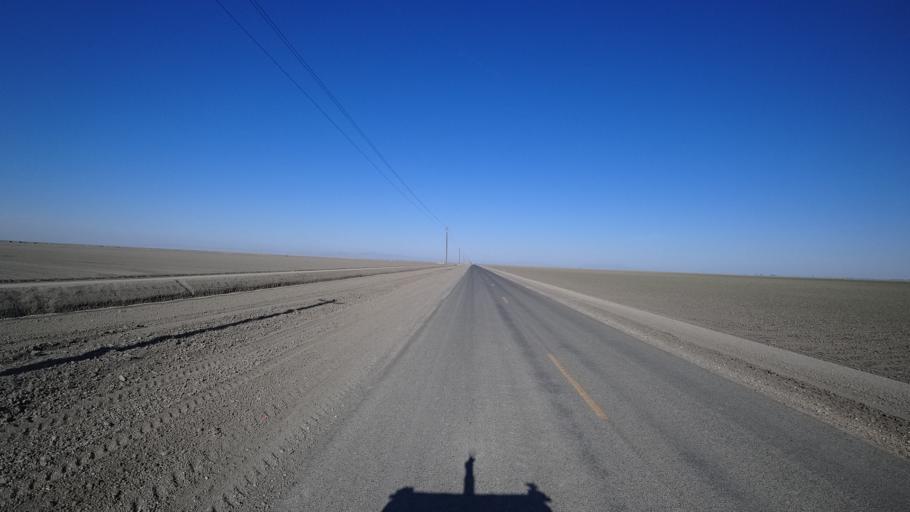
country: US
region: California
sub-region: Kings County
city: Corcoran
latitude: 36.0797
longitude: -119.7103
